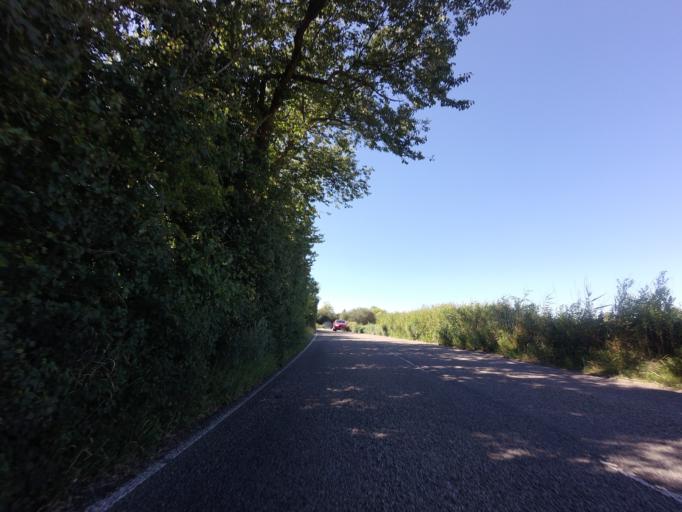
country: GB
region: England
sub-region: Kent
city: Ash
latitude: 51.3161
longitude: 1.2127
